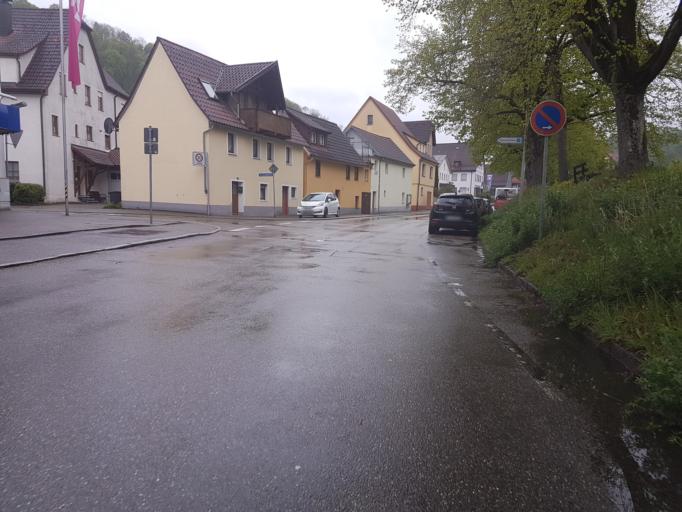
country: DE
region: Baden-Wuerttemberg
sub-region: Freiburg Region
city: Sulz am Neckar
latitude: 48.3628
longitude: 8.6359
